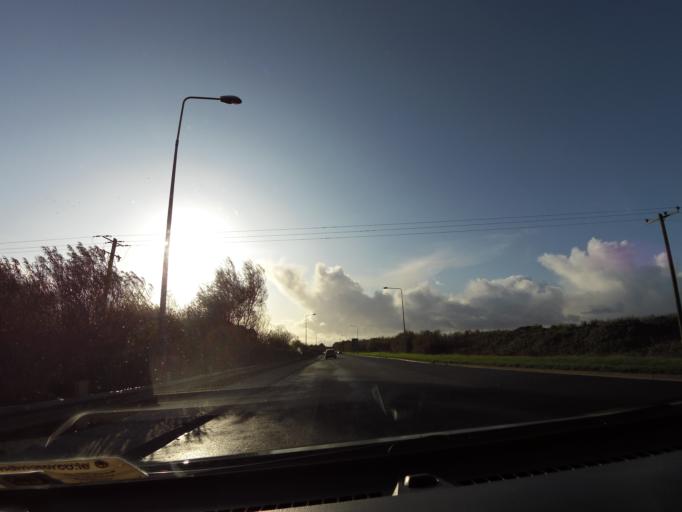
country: IE
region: Munster
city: Moyross
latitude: 52.6488
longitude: -8.6648
